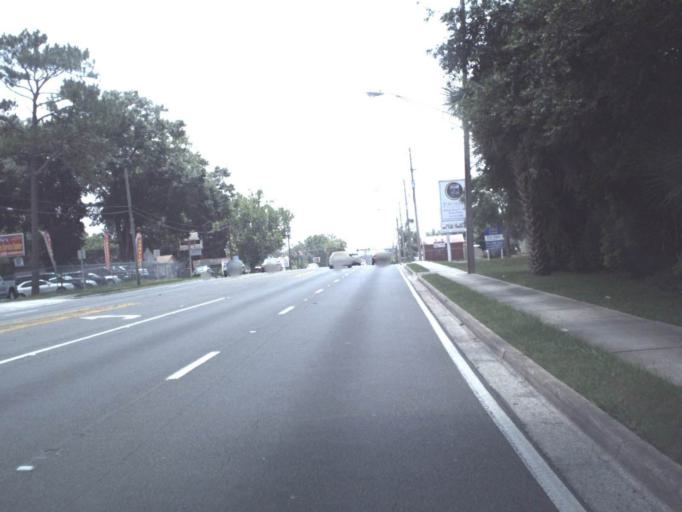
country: US
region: Florida
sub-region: Duval County
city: Jacksonville
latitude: 30.4018
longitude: -81.6843
